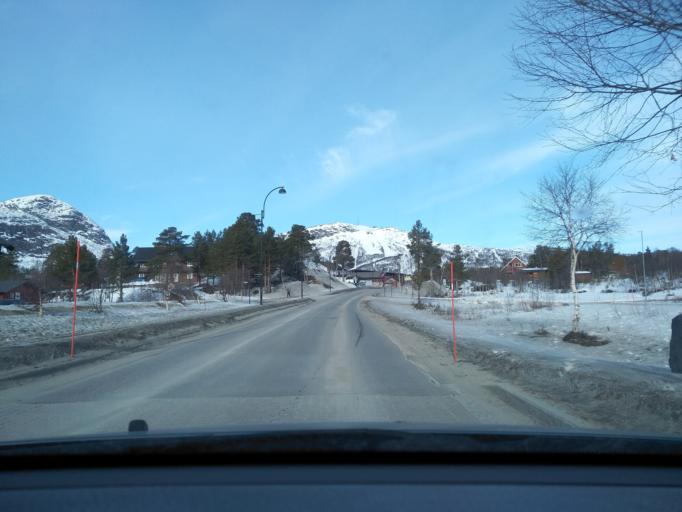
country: NO
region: Aust-Agder
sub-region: Bykle
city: Hovden
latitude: 59.5577
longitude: 7.3584
